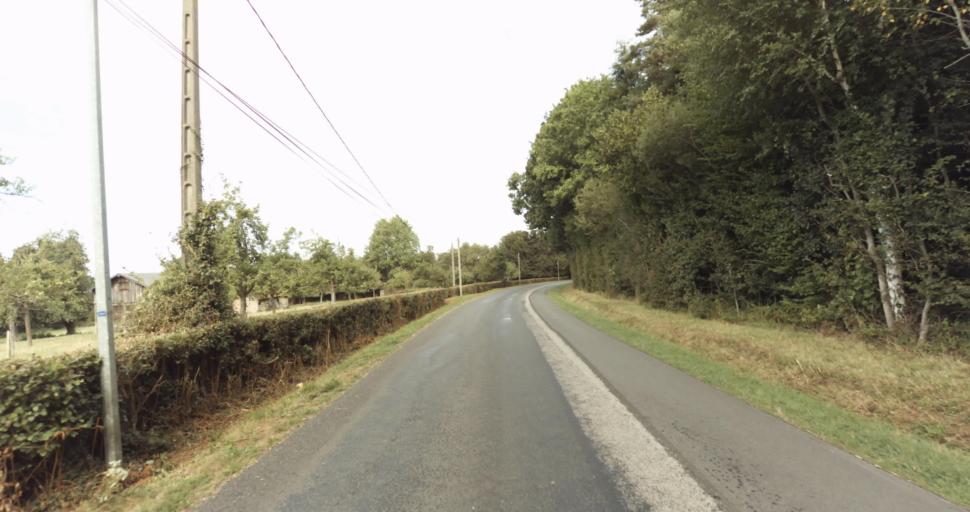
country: FR
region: Lower Normandy
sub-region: Departement de l'Orne
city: Gace
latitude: 48.8171
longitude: 0.2345
